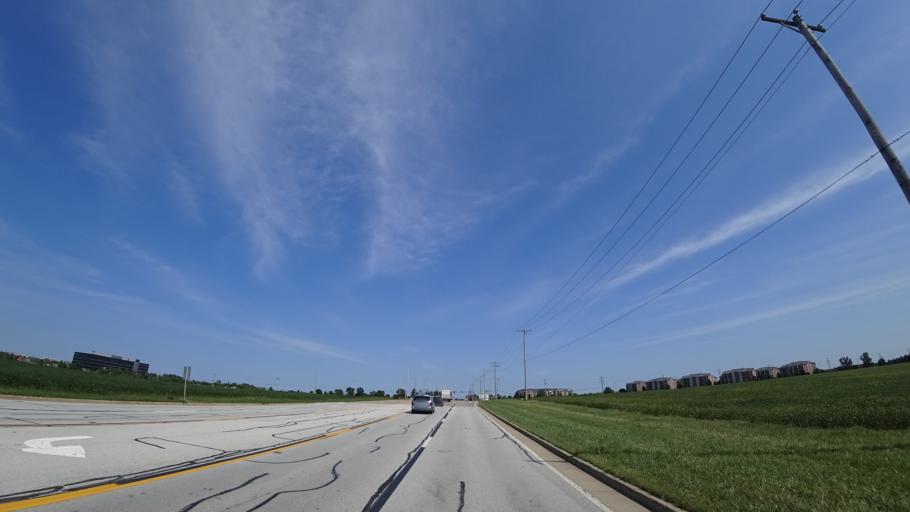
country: US
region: Illinois
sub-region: Will County
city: Frankfort Square
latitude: 41.5436
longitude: -87.8148
